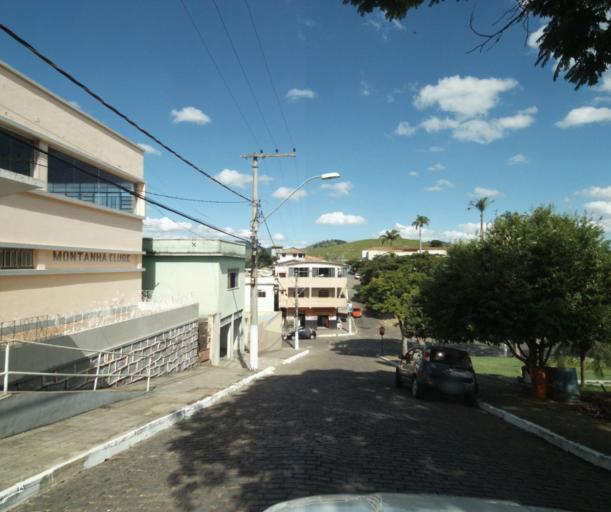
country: BR
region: Espirito Santo
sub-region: Sao Jose Do Calcado
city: Sao Jose do Calcado
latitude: -21.0258
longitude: -41.6537
